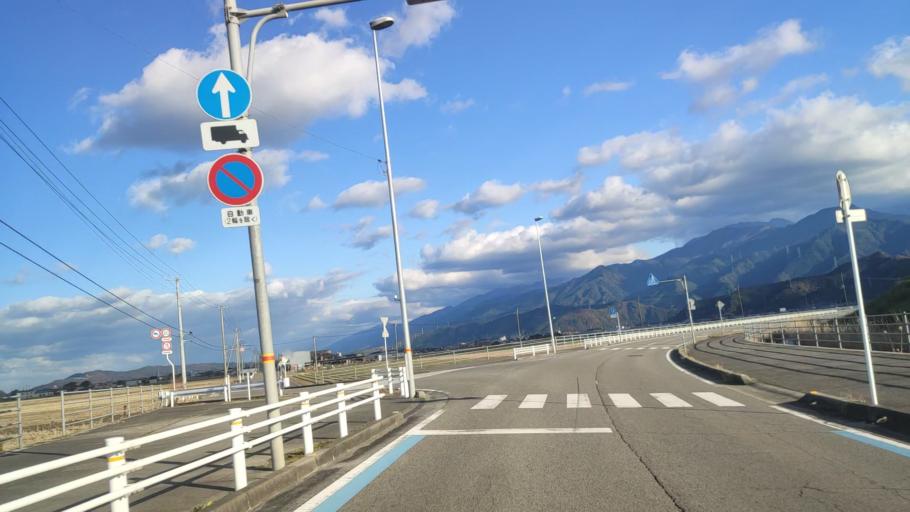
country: JP
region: Ehime
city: Saijo
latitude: 33.9093
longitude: 133.1408
